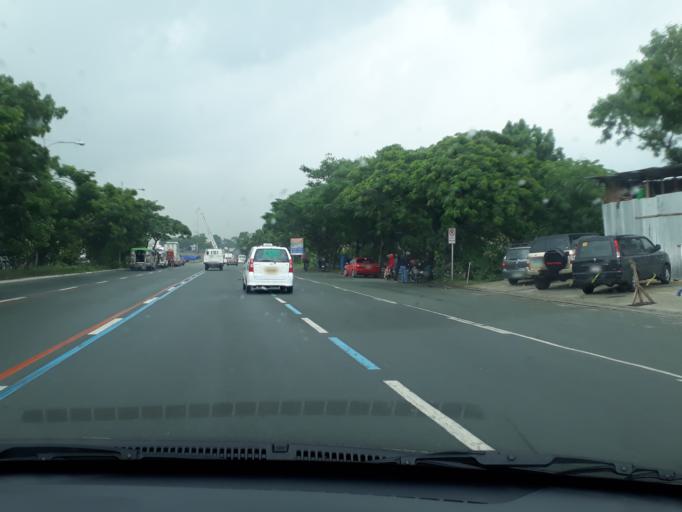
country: PH
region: Metro Manila
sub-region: Makati City
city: Makati City
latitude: 14.5162
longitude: 121.0428
